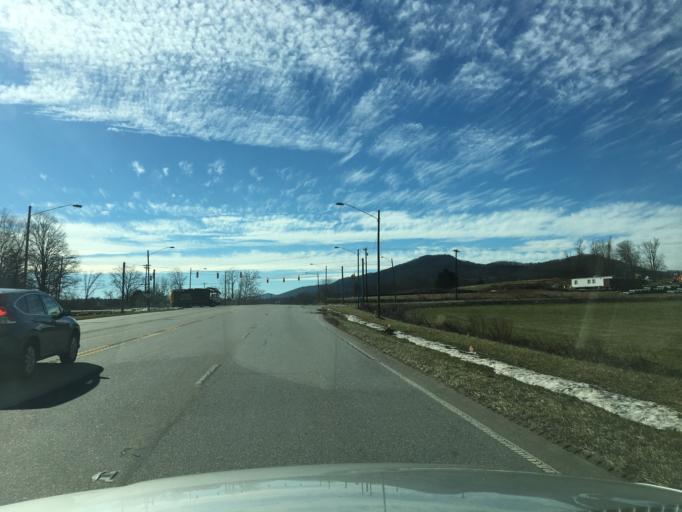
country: US
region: North Carolina
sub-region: Henderson County
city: Mills River
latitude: 35.3767
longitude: -82.5794
